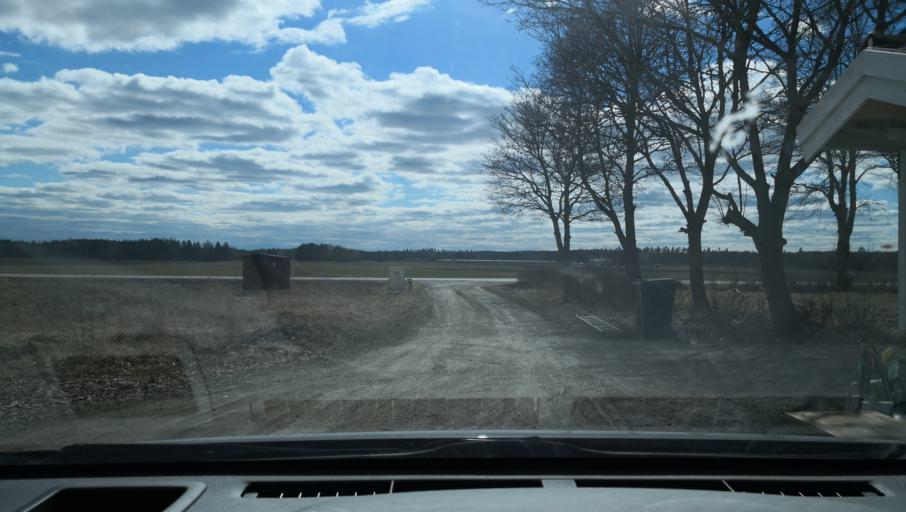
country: SE
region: Vaestmanland
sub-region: Sala Kommun
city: Sala
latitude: 59.8603
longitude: 16.6032
